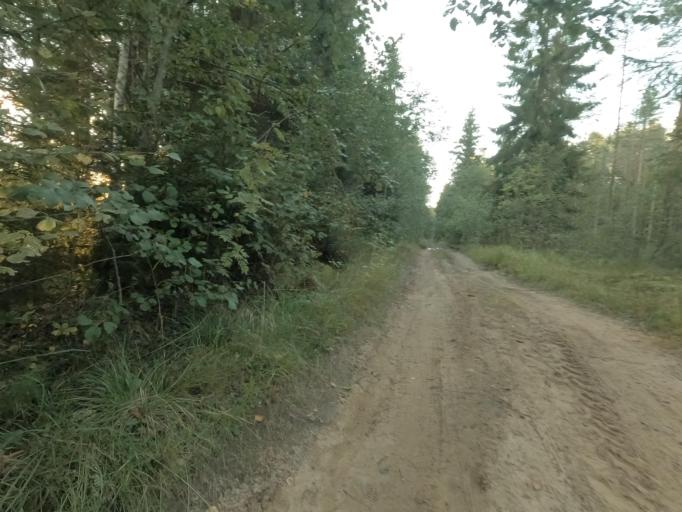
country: RU
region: Leningrad
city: Otradnoye
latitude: 59.8245
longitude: 30.8210
